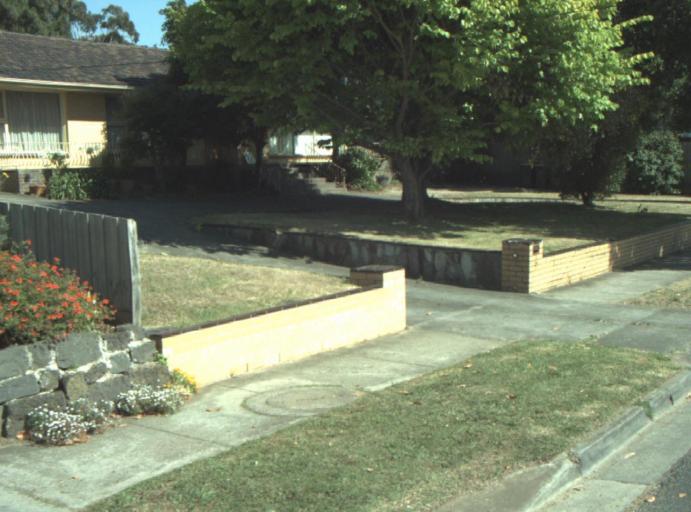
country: AU
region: Victoria
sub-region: Greater Geelong
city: Wandana Heights
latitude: -38.1733
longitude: 144.3182
